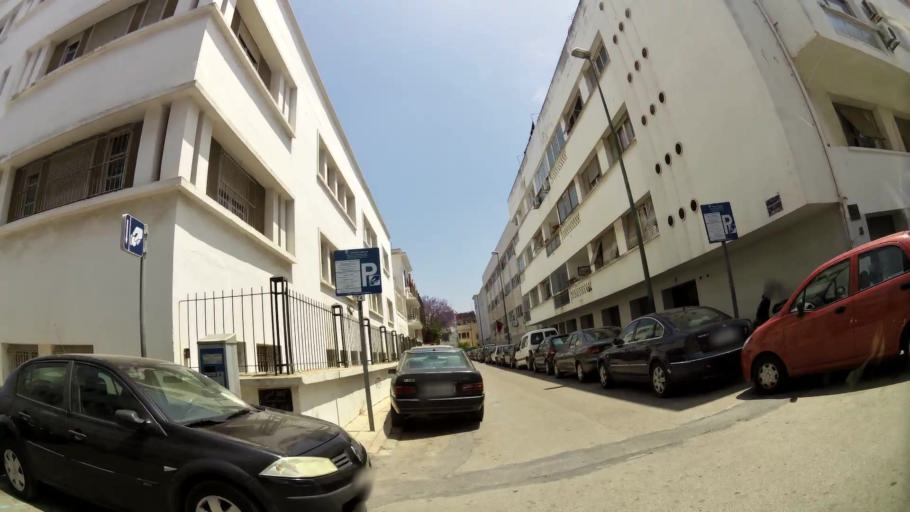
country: MA
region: Rabat-Sale-Zemmour-Zaer
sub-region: Rabat
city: Rabat
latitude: 34.0147
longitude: -6.8320
